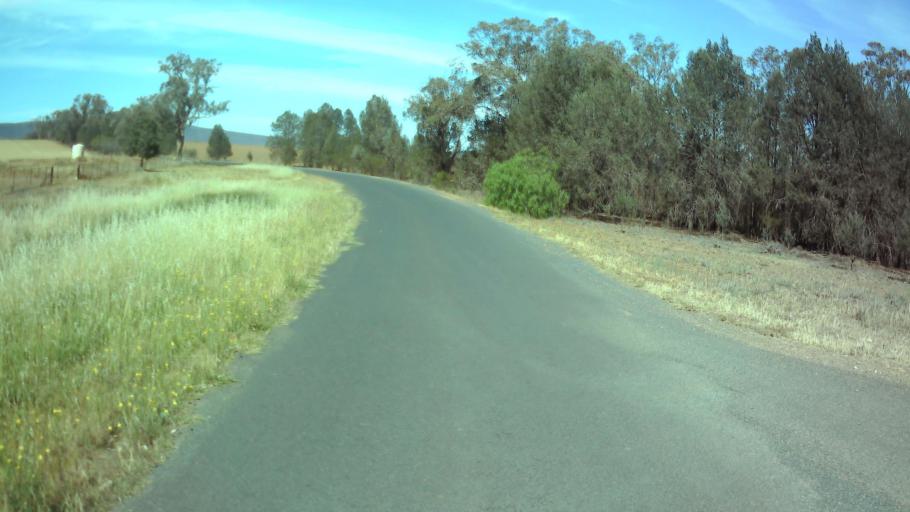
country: AU
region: New South Wales
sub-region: Weddin
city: Grenfell
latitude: -33.9315
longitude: 148.0858
